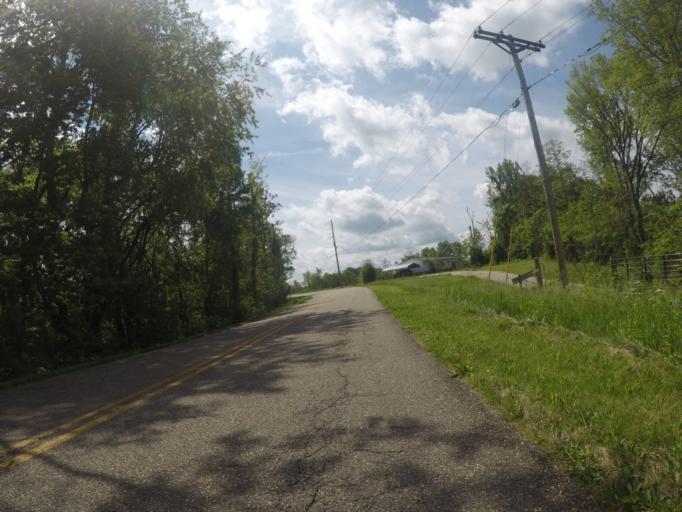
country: US
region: West Virginia
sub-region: Cabell County
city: Huntington
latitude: 38.5404
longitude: -82.4268
